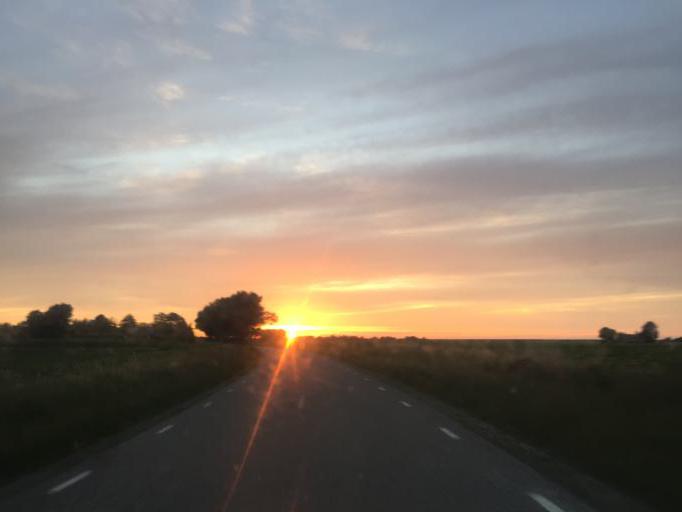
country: NL
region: Friesland
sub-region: Gemeente Dongeradeel
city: Anjum
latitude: 53.3879
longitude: 6.1093
